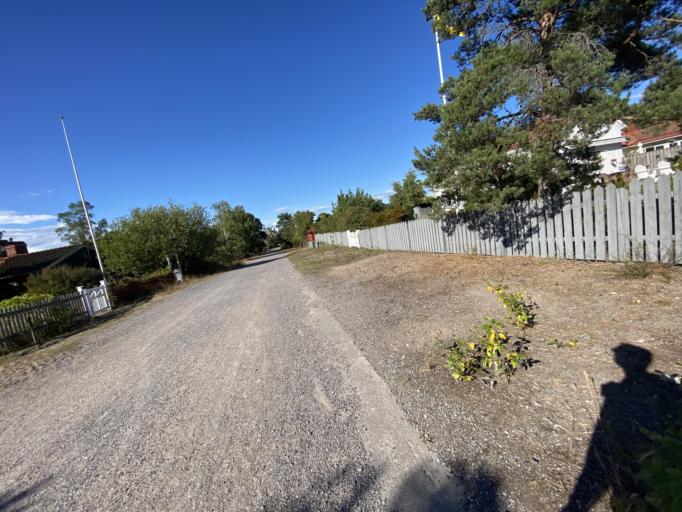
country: SE
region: Stockholm
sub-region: Varmdo Kommun
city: Holo
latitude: 59.2877
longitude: 18.9092
